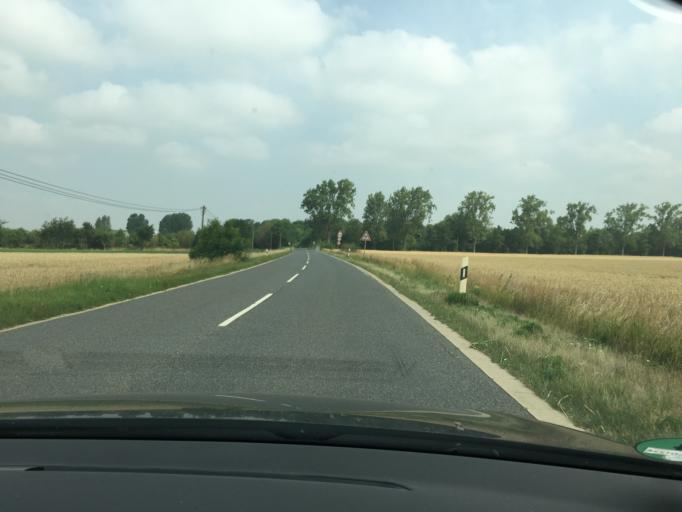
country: DE
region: North Rhine-Westphalia
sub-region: Regierungsbezirk Koln
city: Norvenich
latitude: 50.8154
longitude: 6.5883
